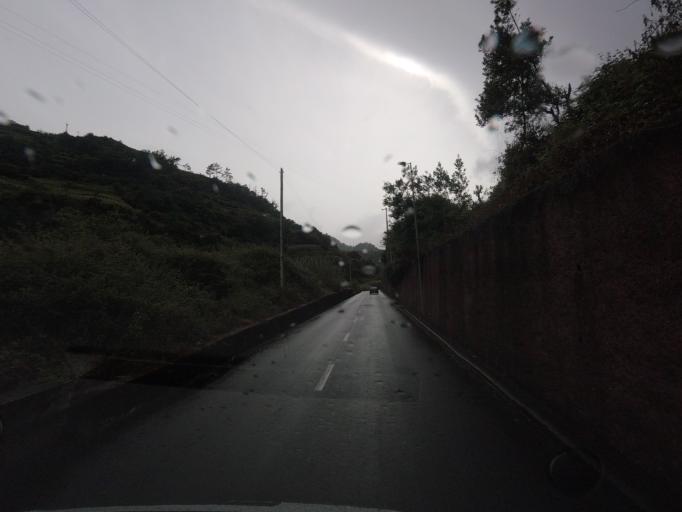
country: PT
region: Madeira
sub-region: Santana
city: Santana
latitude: 32.7718
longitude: -16.8324
